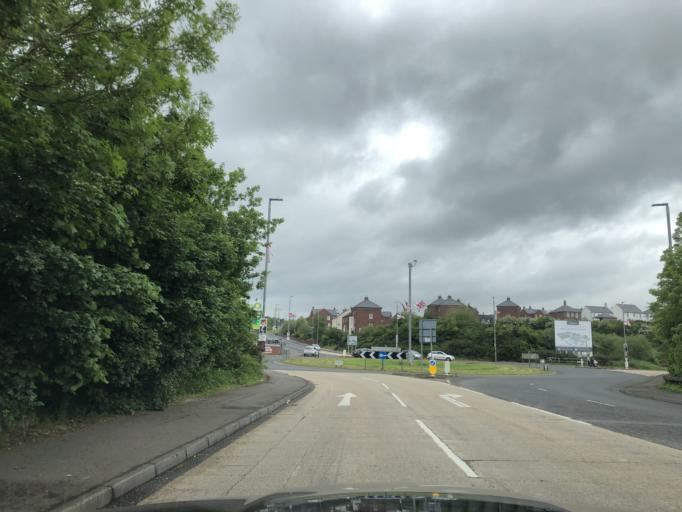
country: GB
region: Northern Ireland
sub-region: Lisburn District
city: Lisburn
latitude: 54.5280
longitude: -6.0728
